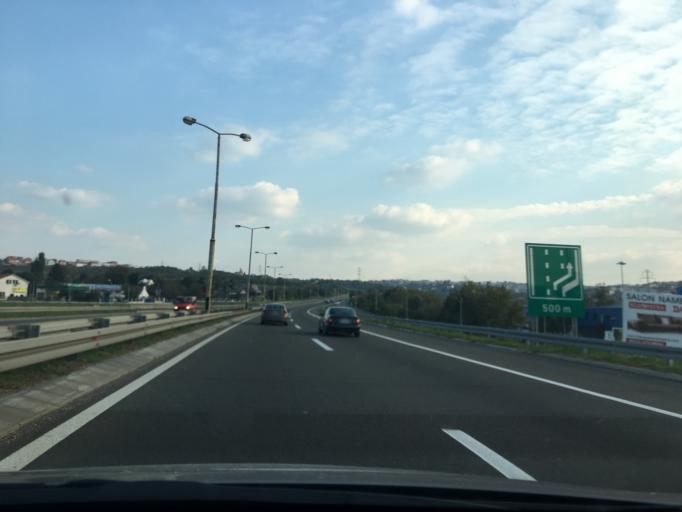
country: RS
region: Central Serbia
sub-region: Belgrade
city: Zvezdara
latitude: 44.7734
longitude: 20.5183
